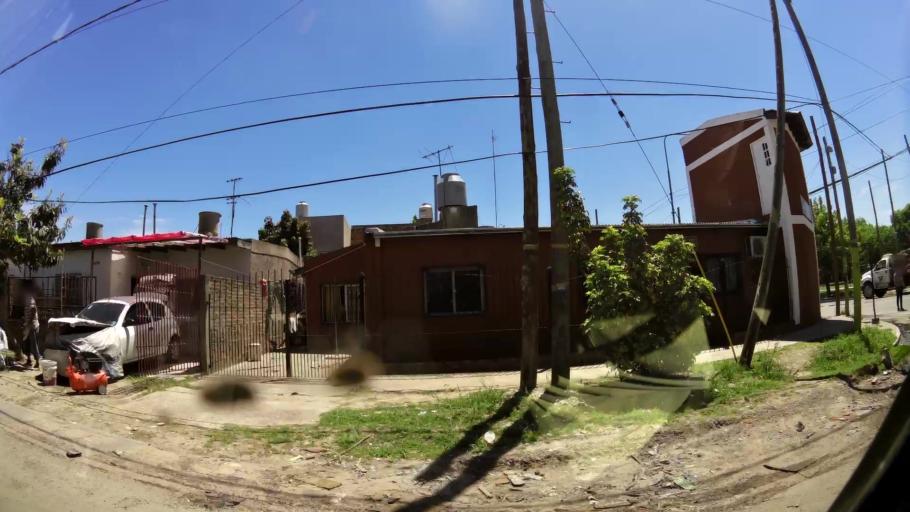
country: AR
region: Buenos Aires
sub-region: Partido de Quilmes
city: Quilmes
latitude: -34.7191
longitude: -58.3199
